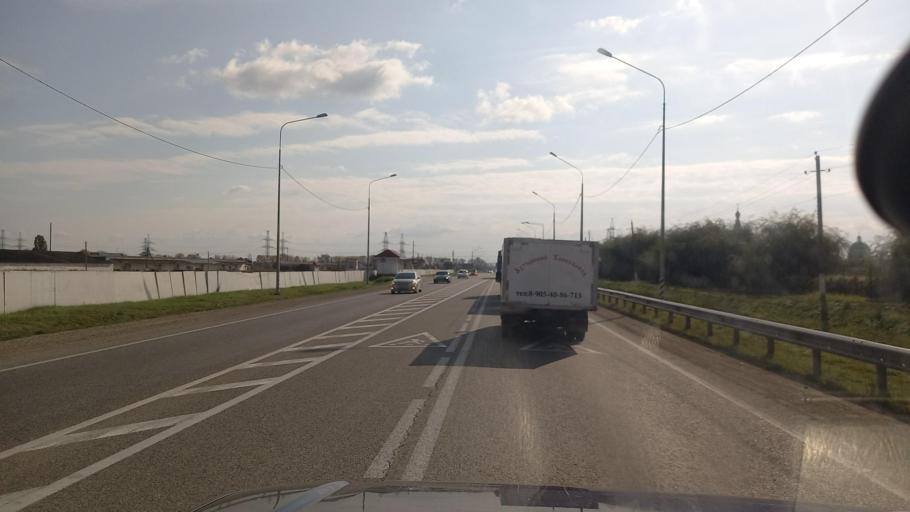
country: RU
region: Krasnodarskiy
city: Novoukrainskiy
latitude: 44.9074
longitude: 38.0252
